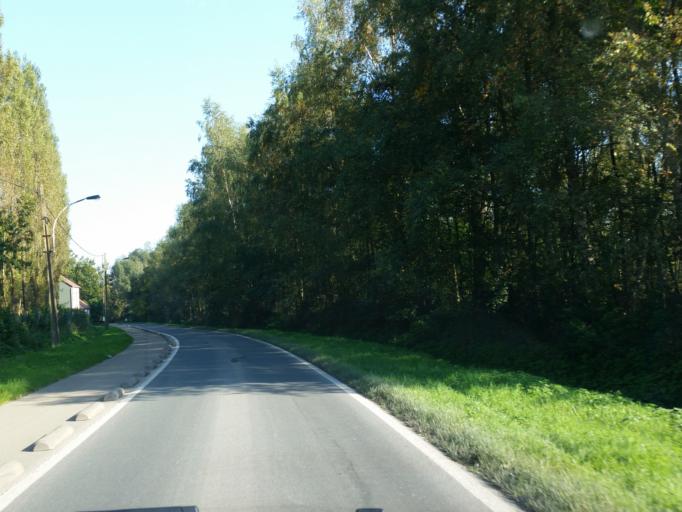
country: BE
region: Flanders
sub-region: Provincie Antwerpen
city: Rumst
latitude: 51.0897
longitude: 4.4284
